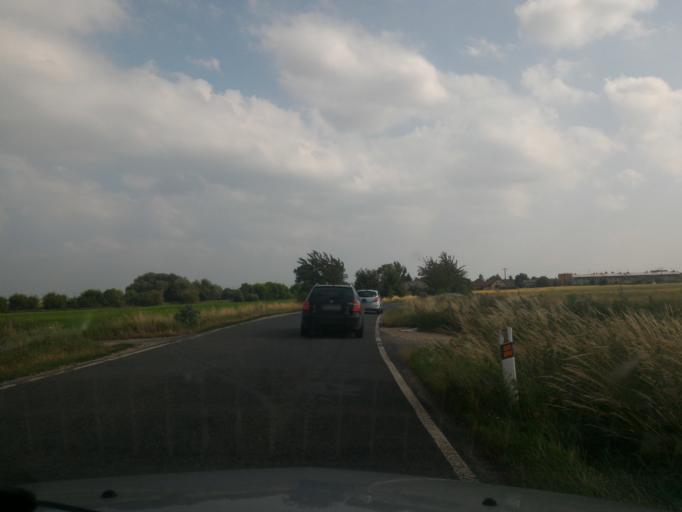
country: CZ
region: Central Bohemia
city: Loucen
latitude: 50.2476
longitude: 15.0238
